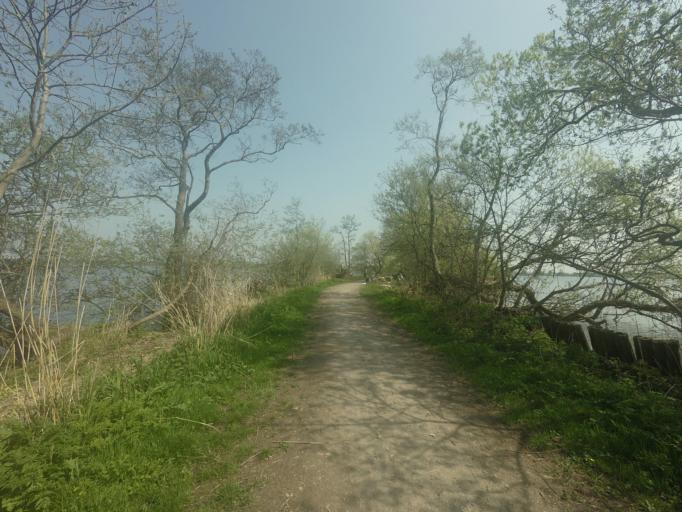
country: NL
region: North Holland
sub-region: Gemeente Wijdemeren
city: Oud-Loosdrecht
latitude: 52.2189
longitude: 5.0593
